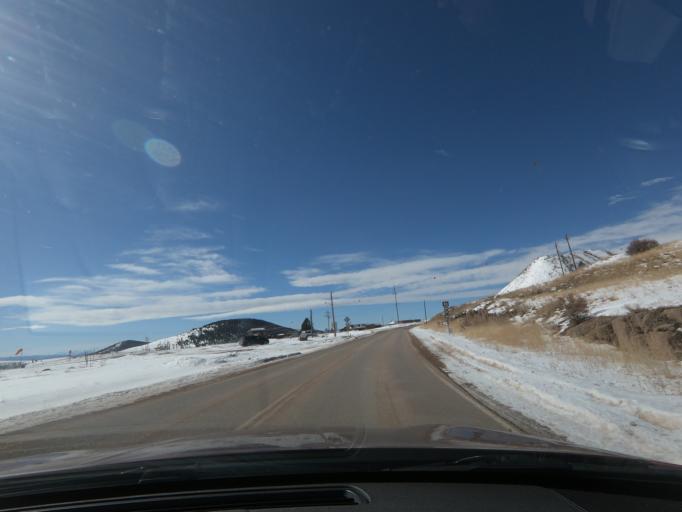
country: US
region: Colorado
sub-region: Teller County
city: Cripple Creek
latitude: 38.7111
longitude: -105.1325
